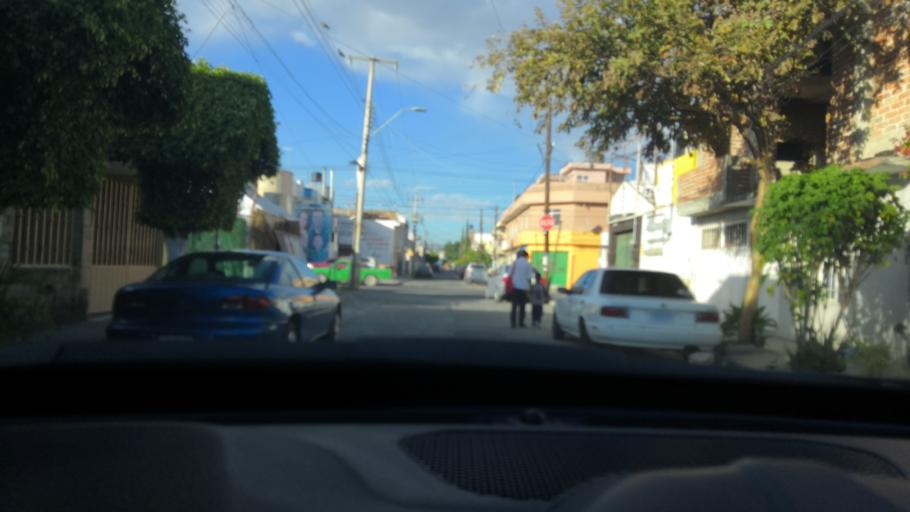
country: MX
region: Guanajuato
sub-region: Leon
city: San Jose de Duran (Los Troncoso)
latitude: 21.0929
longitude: -101.6523
